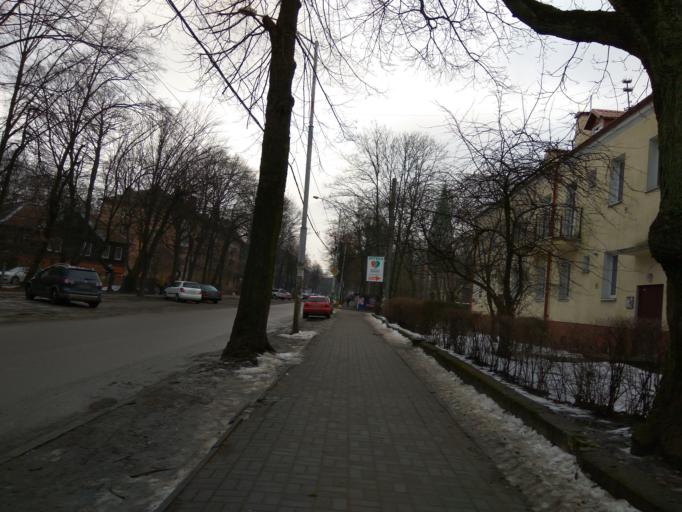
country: RU
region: Kaliningrad
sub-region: Gorod Kaliningrad
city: Kaliningrad
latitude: 54.7183
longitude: 20.4723
